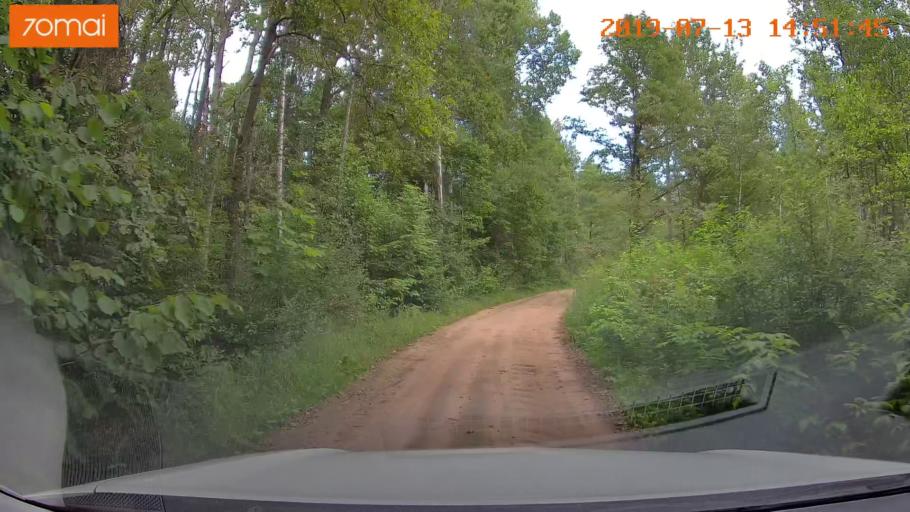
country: BY
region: Mogilev
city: Asipovichy
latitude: 53.2115
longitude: 28.7508
